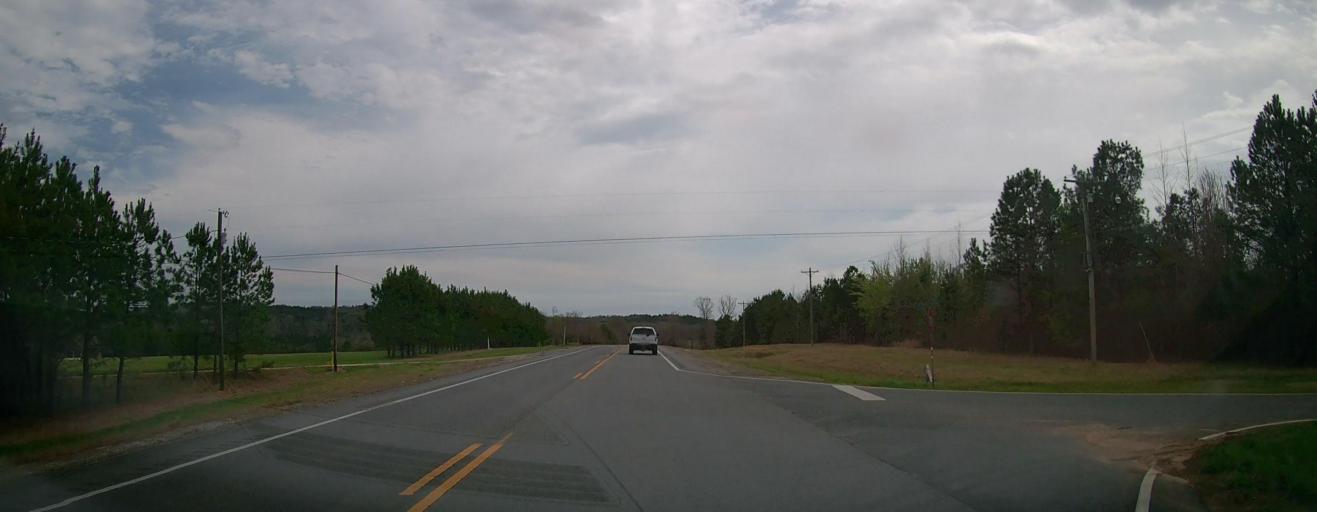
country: US
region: Alabama
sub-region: Marion County
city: Guin
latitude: 34.0070
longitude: -87.9338
